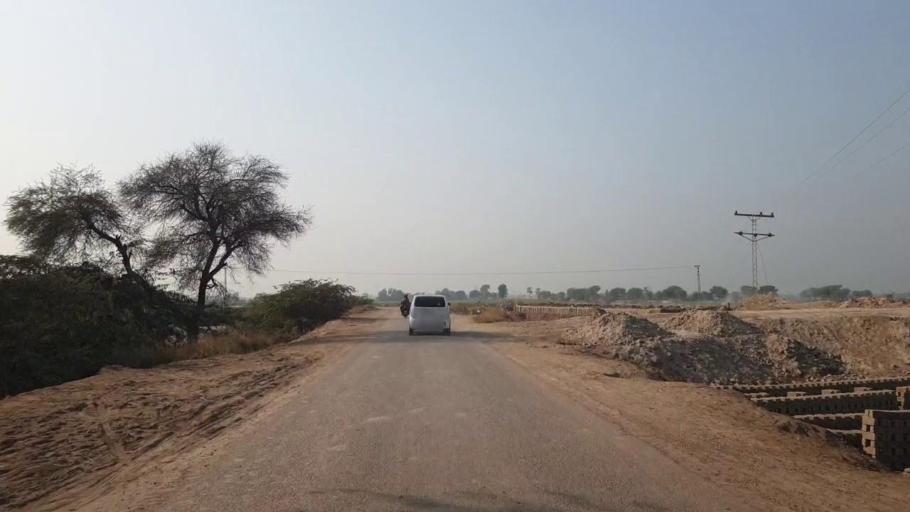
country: PK
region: Sindh
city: Shahdadpur
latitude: 25.9655
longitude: 68.5773
